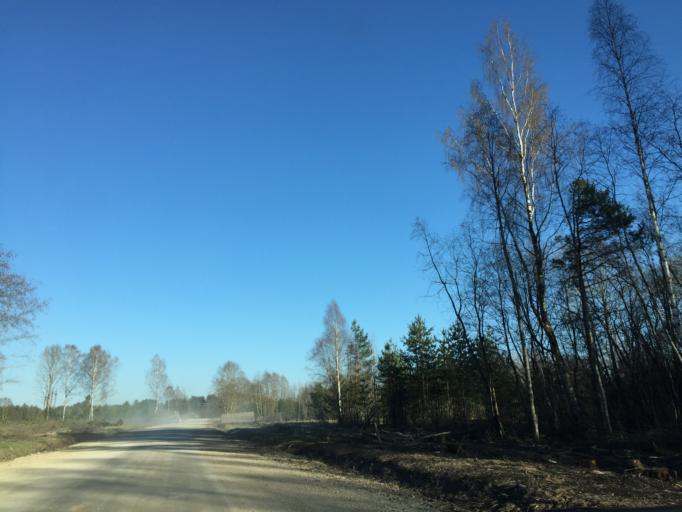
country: EE
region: Ida-Virumaa
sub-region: Sillamaee linn
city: Sillamae
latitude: 59.0862
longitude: 27.7615
